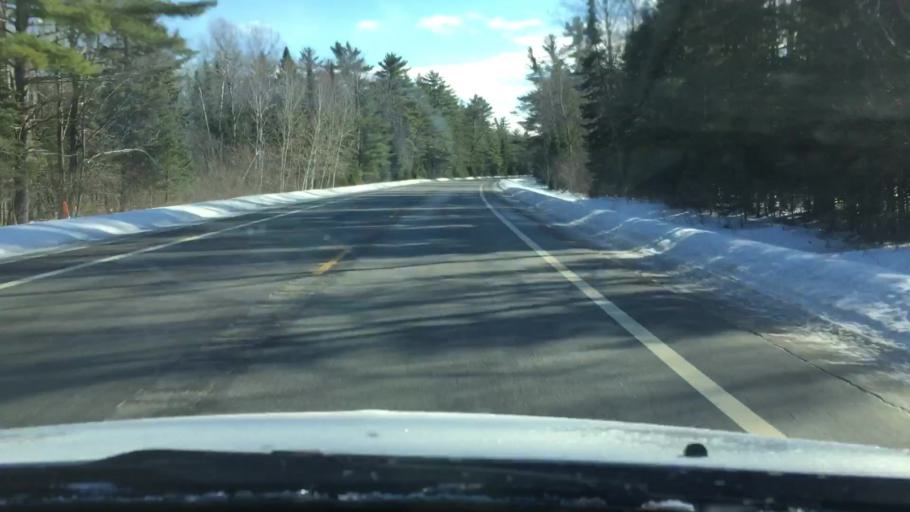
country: US
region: Michigan
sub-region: Charlevoix County
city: East Jordan
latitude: 45.0550
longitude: -85.0728
